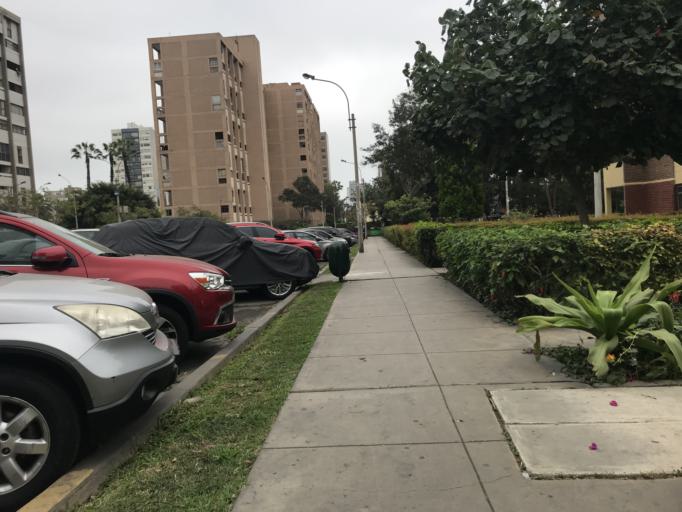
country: PE
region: Lima
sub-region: Lima
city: San Isidro
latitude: -12.0894
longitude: -77.0550
